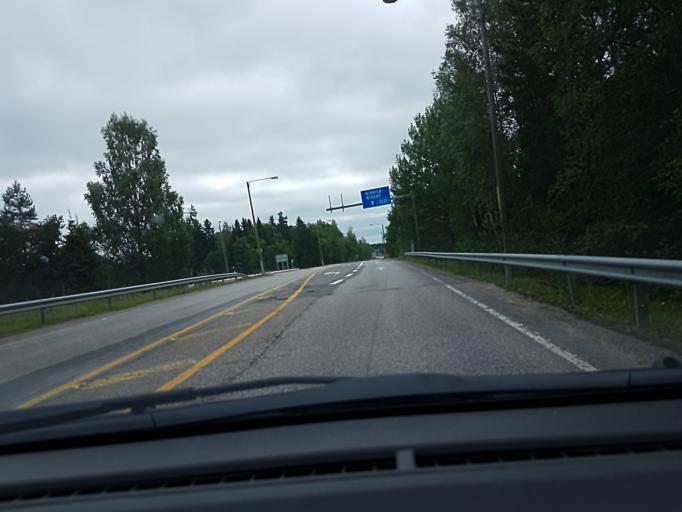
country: FI
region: Uusimaa
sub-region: Helsinki
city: Sibbo
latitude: 60.3701
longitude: 25.2362
